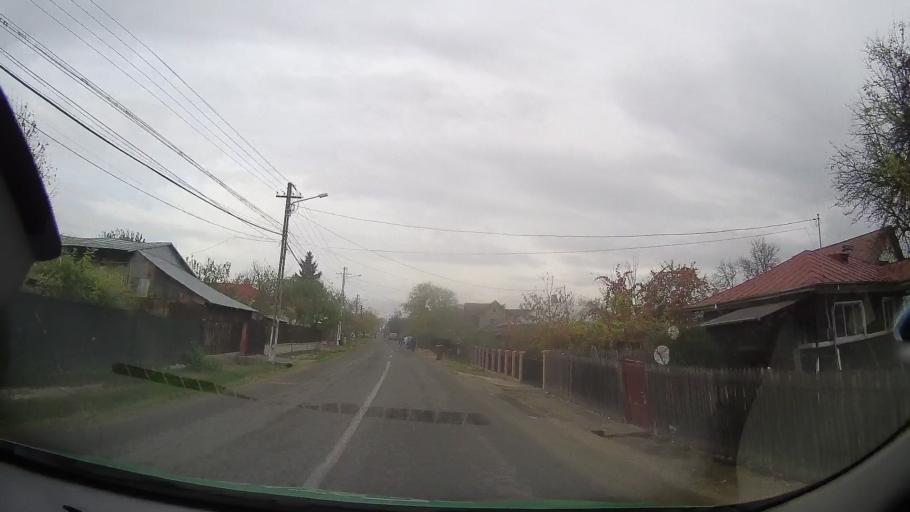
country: RO
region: Prahova
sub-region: Comuna Berceni
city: Berceni
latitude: 44.9332
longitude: 26.1238
